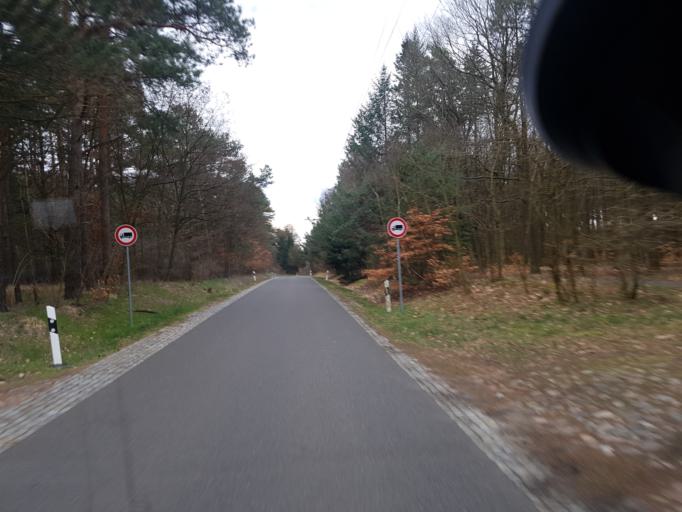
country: DE
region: Brandenburg
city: Mixdorf
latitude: 52.1876
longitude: 14.4293
